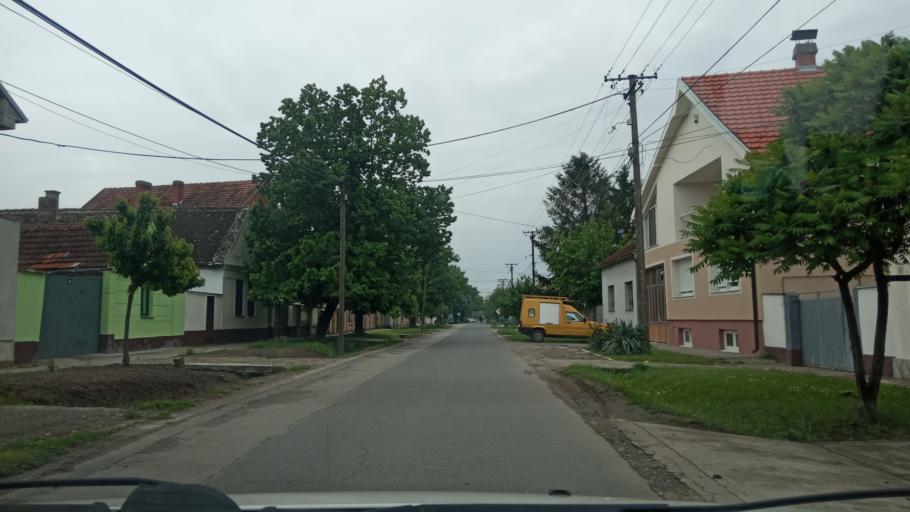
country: RS
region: Autonomna Pokrajina Vojvodina
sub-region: Sremski Okrug
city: Stara Pazova
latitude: 44.9919
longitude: 20.1530
